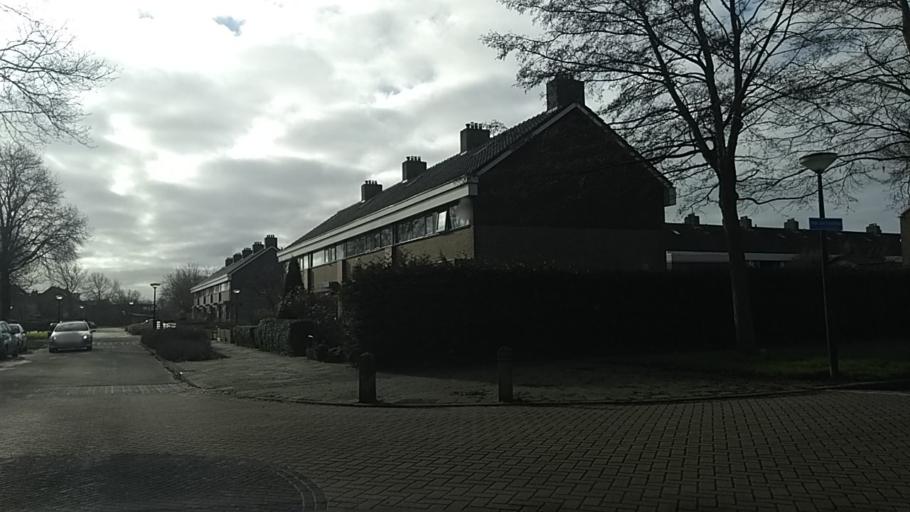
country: NL
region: Friesland
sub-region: Gemeente Harlingen
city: Harlingen
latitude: 53.1653
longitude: 5.4387
